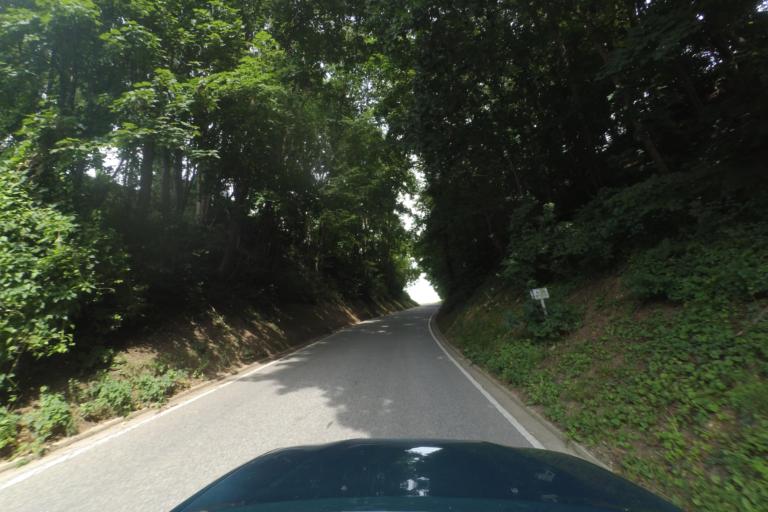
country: DE
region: Bavaria
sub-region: Lower Bavaria
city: Oberporing
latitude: 48.6961
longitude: 12.8105
